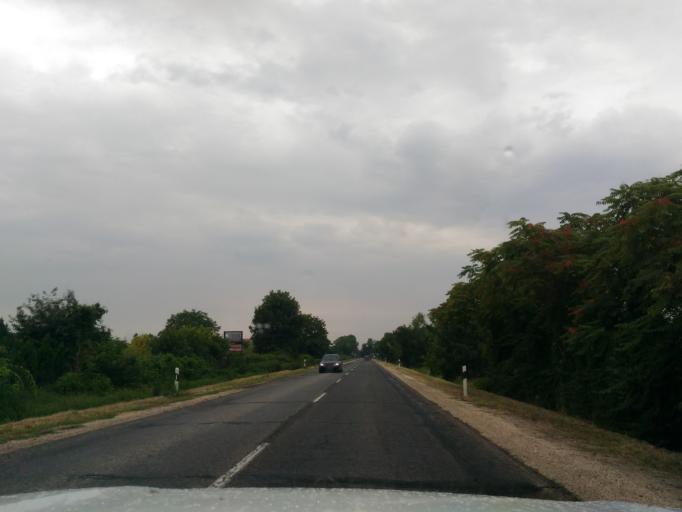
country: HU
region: Pest
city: Dabas
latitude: 47.2146
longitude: 19.2795
